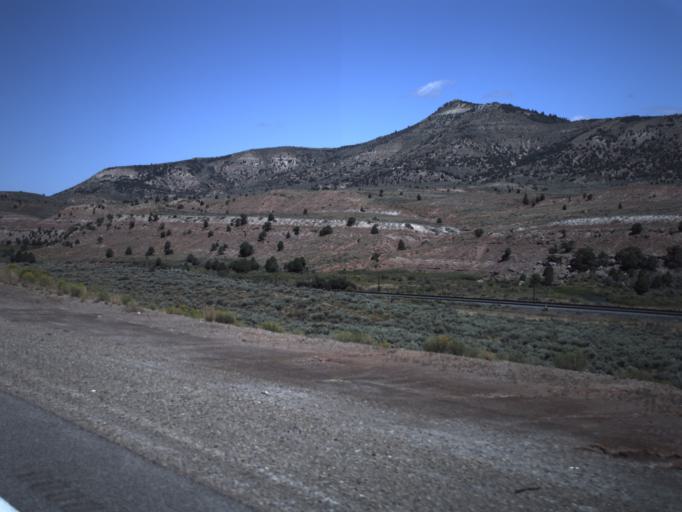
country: US
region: Utah
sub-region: Carbon County
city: Helper
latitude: 39.8386
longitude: -110.9831
